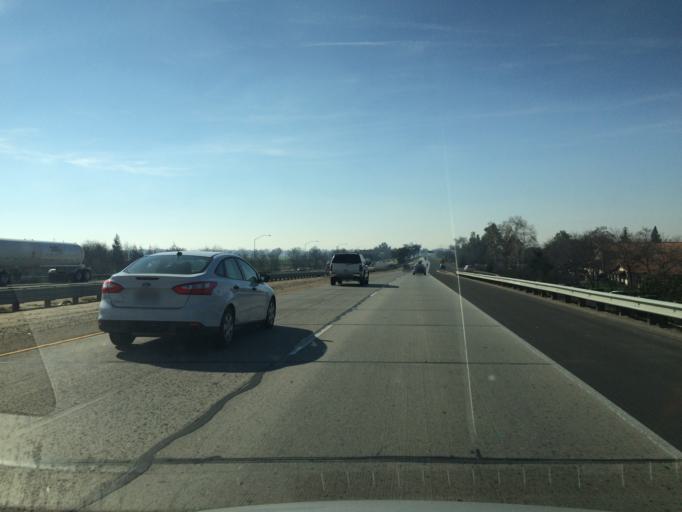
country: US
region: California
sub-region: Tulare County
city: Visalia
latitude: 36.3274
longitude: -119.3505
